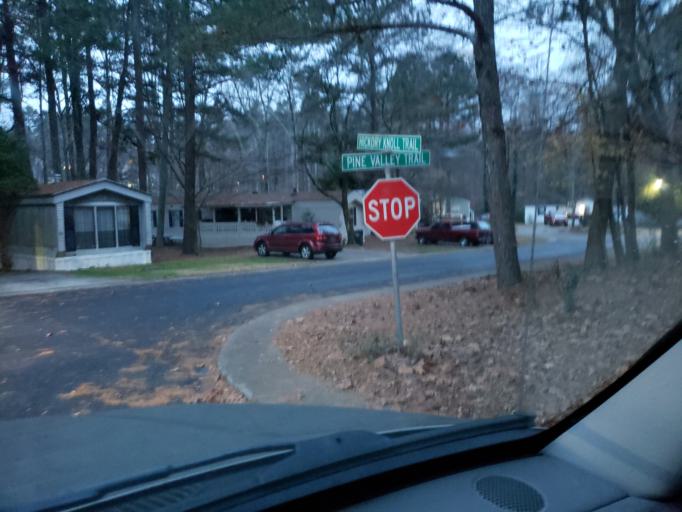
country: US
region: Georgia
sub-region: Cobb County
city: Kennesaw
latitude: 34.0205
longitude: -84.6327
